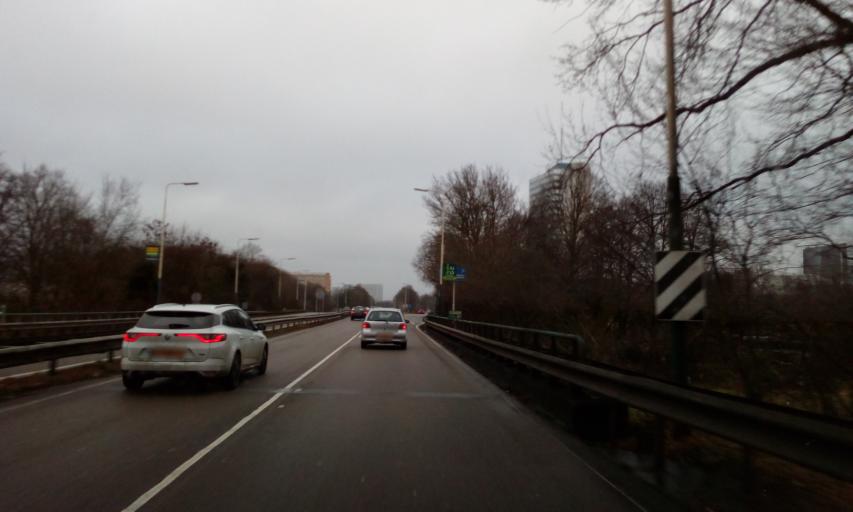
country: NL
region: Utrecht
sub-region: Gemeente Utrecht
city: Lunetten
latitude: 52.0750
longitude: 5.1398
